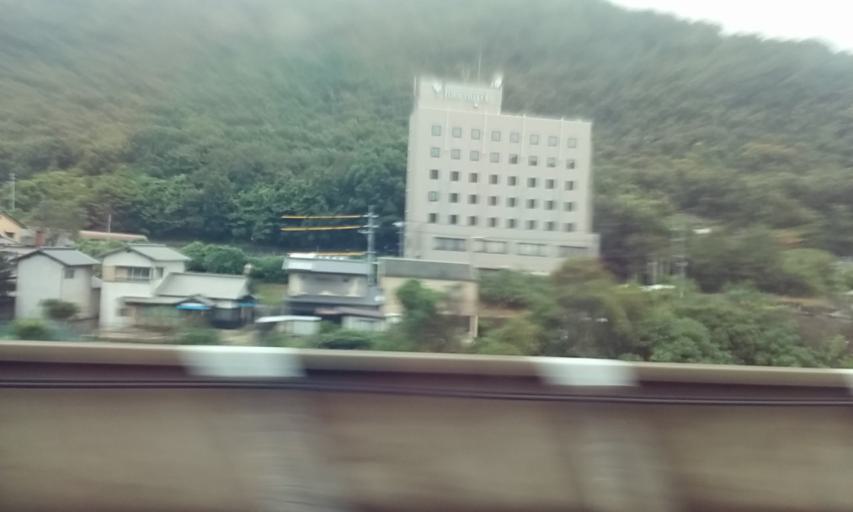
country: JP
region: Okayama
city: Okayama-shi
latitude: 34.7395
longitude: 134.1511
